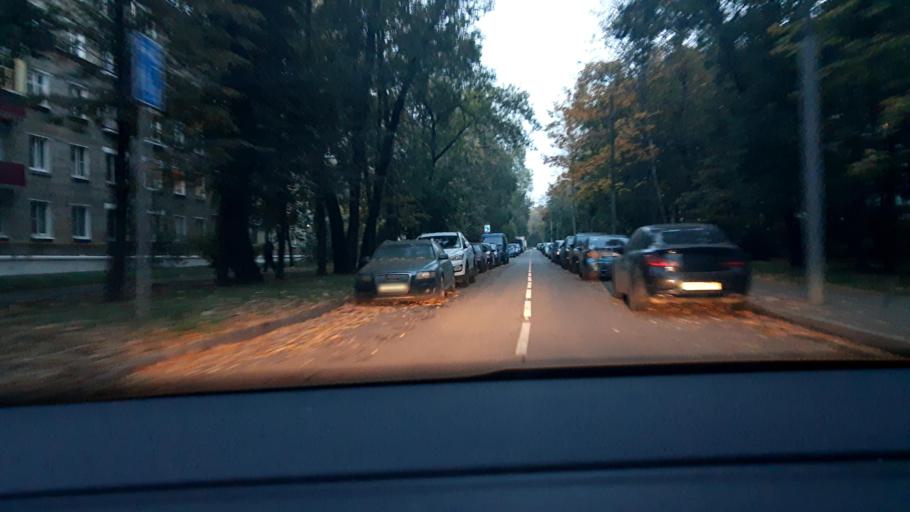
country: RU
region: Moscow
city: Likhobory
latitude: 55.8133
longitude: 37.5639
